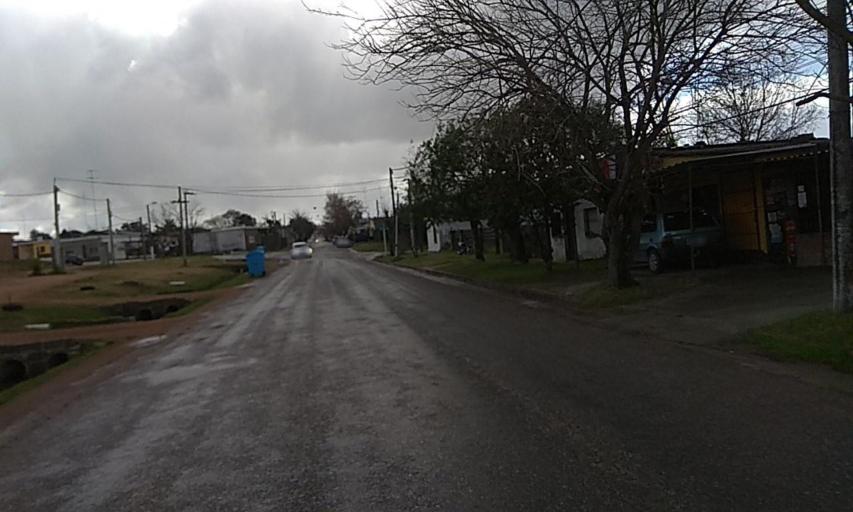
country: UY
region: Florida
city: Florida
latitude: -34.1026
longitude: -56.2248
